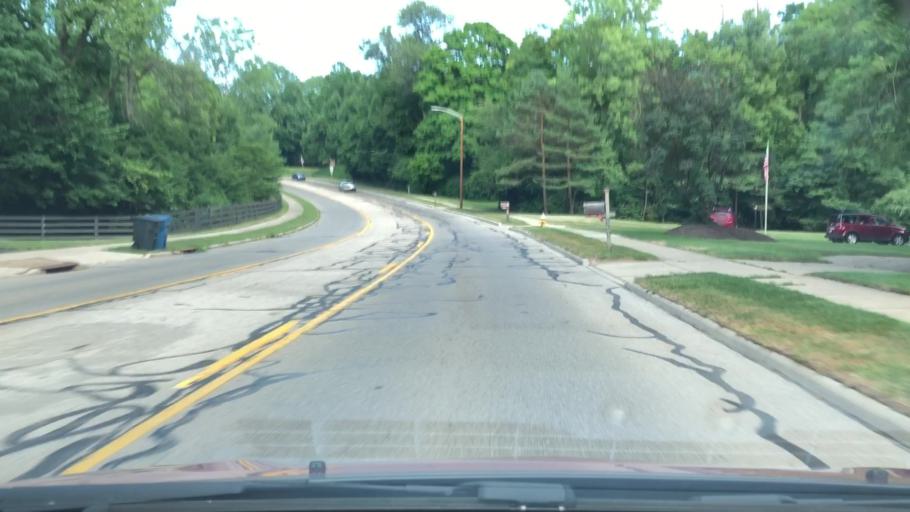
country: US
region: Ohio
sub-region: Montgomery County
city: Centerville
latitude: 39.6585
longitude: -84.1513
